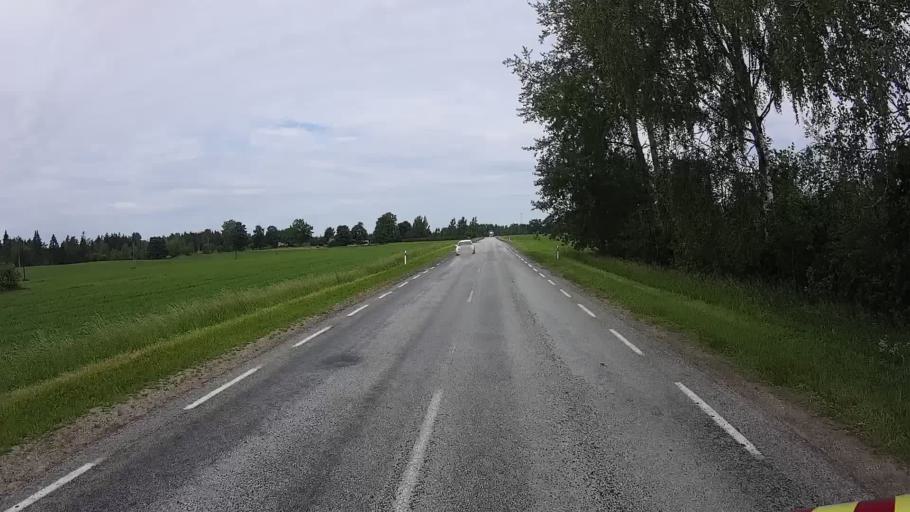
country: EE
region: Viljandimaa
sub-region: Karksi vald
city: Karksi-Nuia
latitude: 58.2256
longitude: 25.6107
